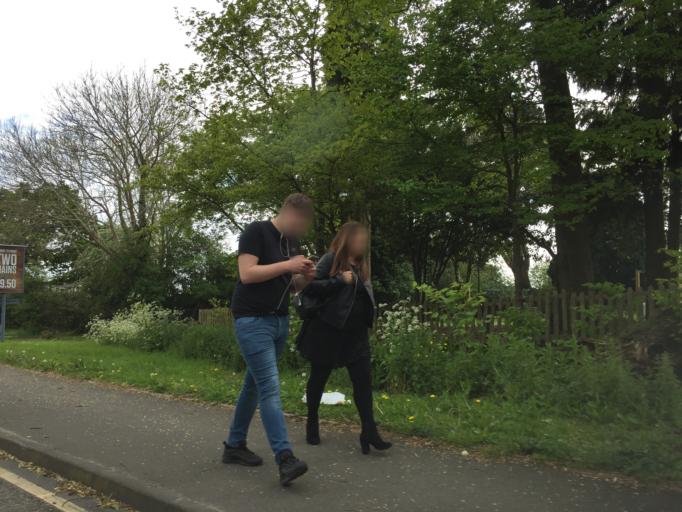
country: GB
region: Wales
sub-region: Caerphilly County Borough
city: Caerphilly
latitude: 51.5303
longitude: -3.2035
